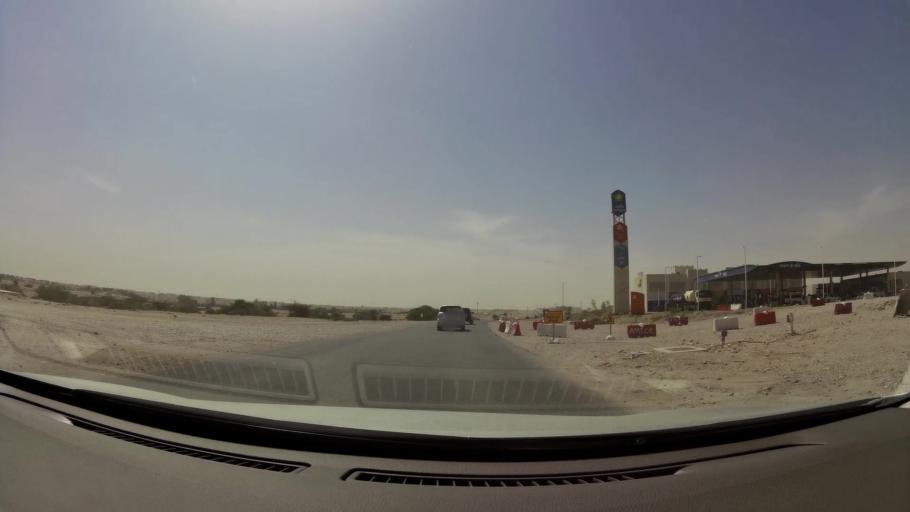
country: QA
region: Baladiyat ar Rayyan
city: Ar Rayyan
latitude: 25.2639
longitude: 51.4060
